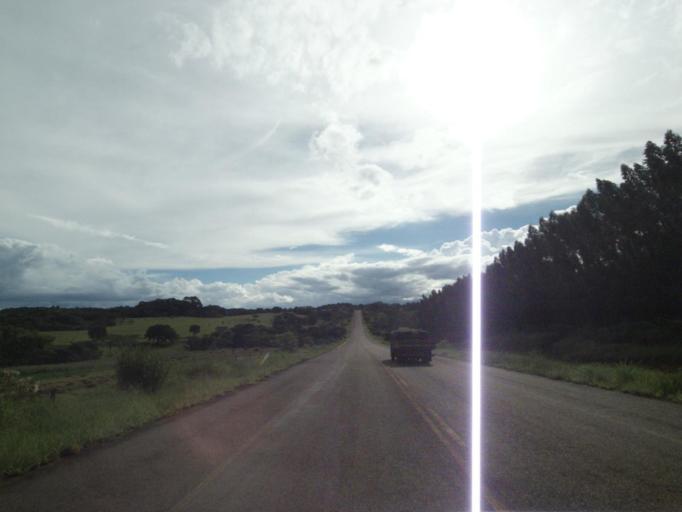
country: BR
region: Goias
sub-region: Jaragua
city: Jaragua
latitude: -15.8827
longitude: -49.4444
